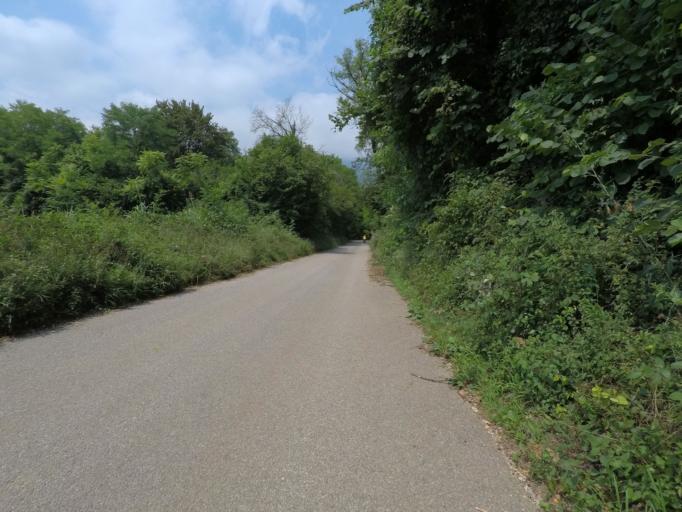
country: IT
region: Friuli Venezia Giulia
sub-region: Provincia di Pordenone
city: Marsure
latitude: 46.1073
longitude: 12.6152
